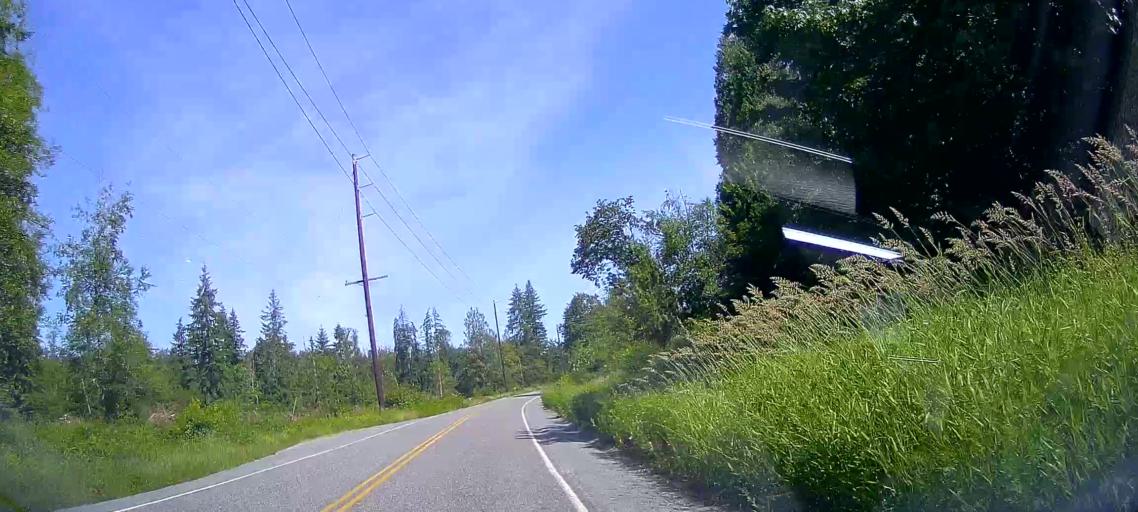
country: US
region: Washington
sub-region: Skagit County
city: Burlington
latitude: 48.5423
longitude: -122.3121
